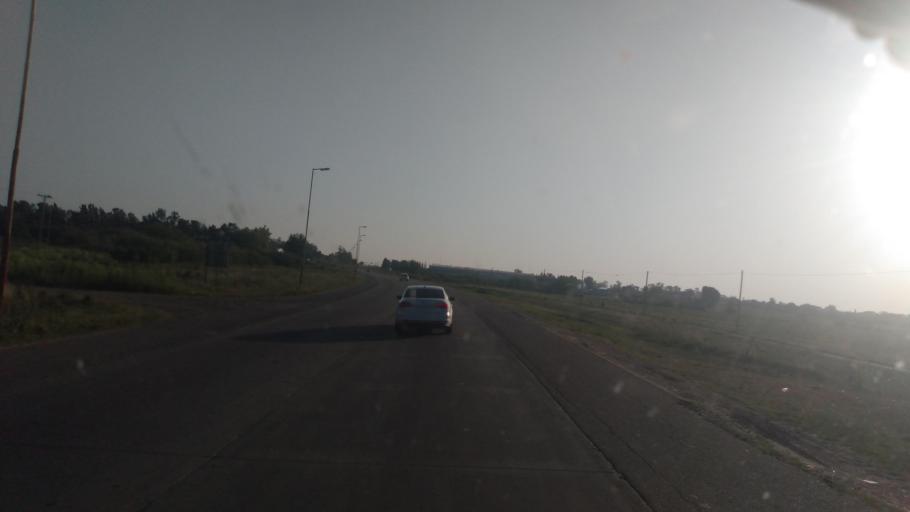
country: AR
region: Buenos Aires
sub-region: Partido de Campana
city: Campana
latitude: -34.1938
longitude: -58.9508
